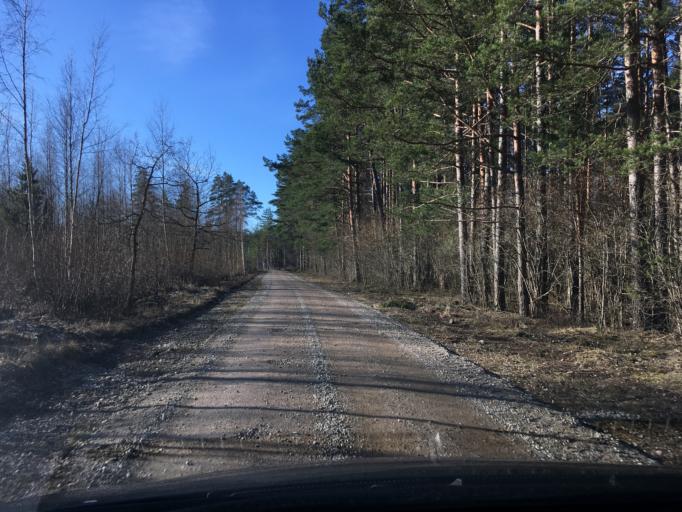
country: EE
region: Laeaene
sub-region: Lihula vald
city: Lihula
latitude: 58.5710
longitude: 23.6938
